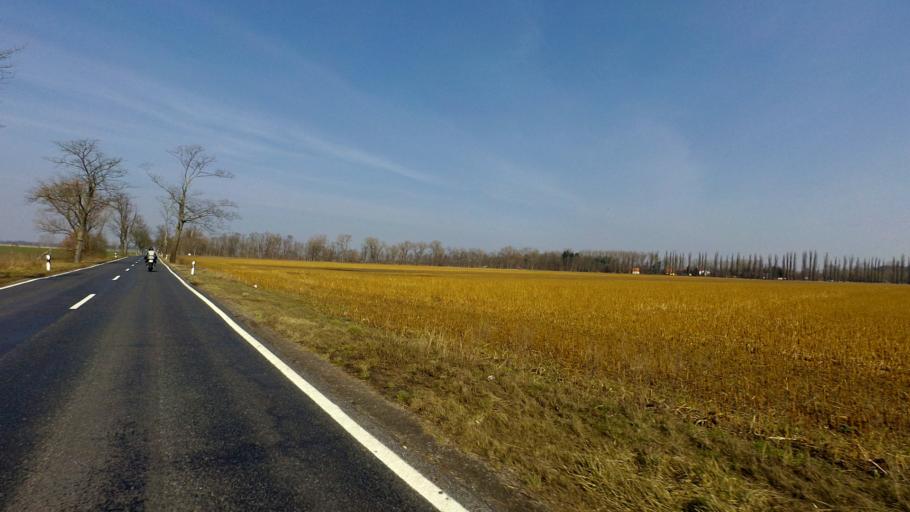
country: DE
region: Brandenburg
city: Ketzin
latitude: 52.4338
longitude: 12.8606
